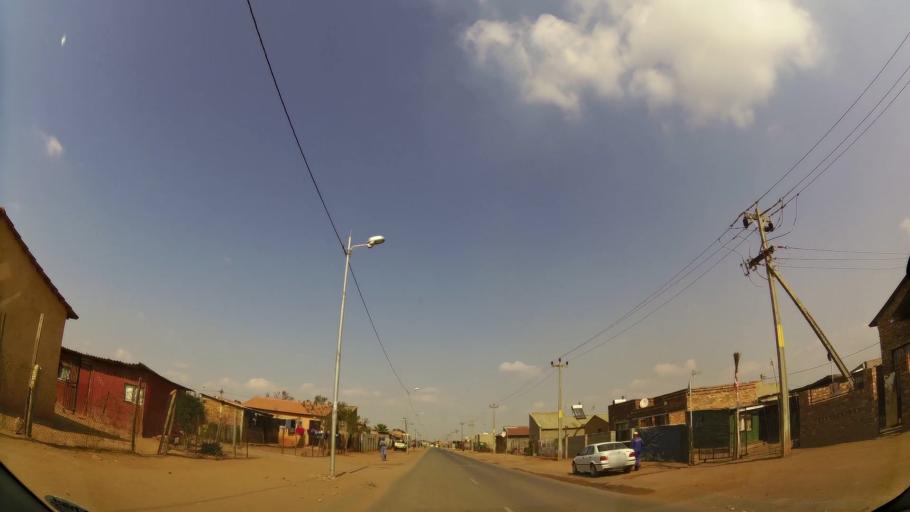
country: ZA
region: Gauteng
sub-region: Ekurhuleni Metropolitan Municipality
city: Springs
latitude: -26.1174
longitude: 28.4843
